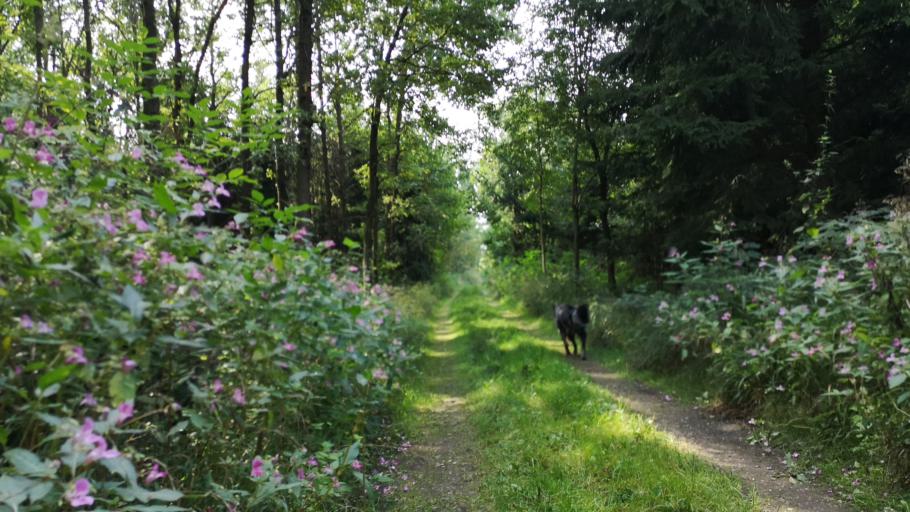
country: DE
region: Bavaria
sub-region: Upper Bavaria
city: Poing
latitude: 48.1794
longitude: 11.8288
